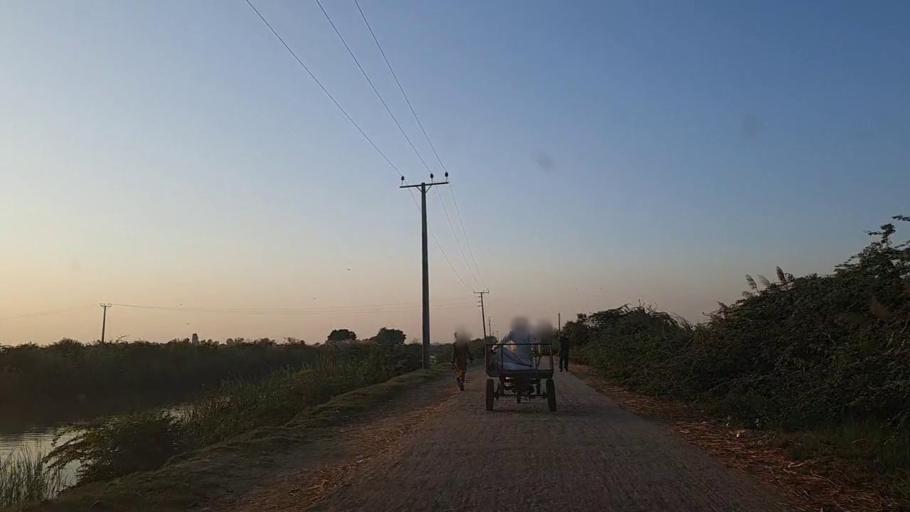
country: PK
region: Sindh
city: Thatta
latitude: 24.7939
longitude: 67.9567
